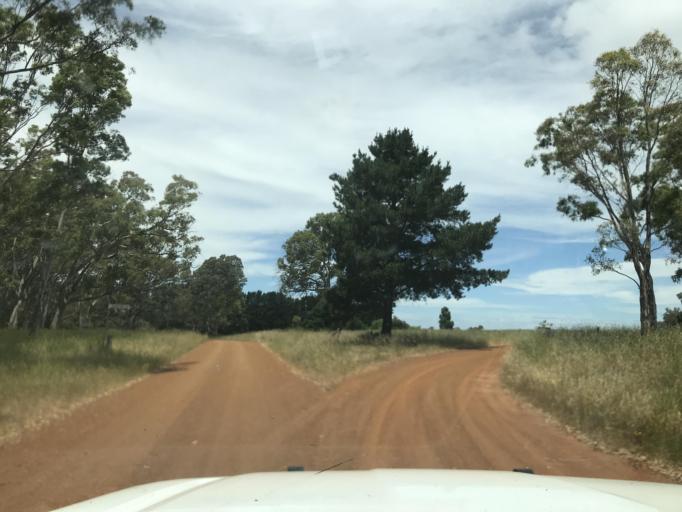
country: AU
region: South Australia
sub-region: Wattle Range
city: Penola
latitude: -37.1570
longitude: 141.5077
